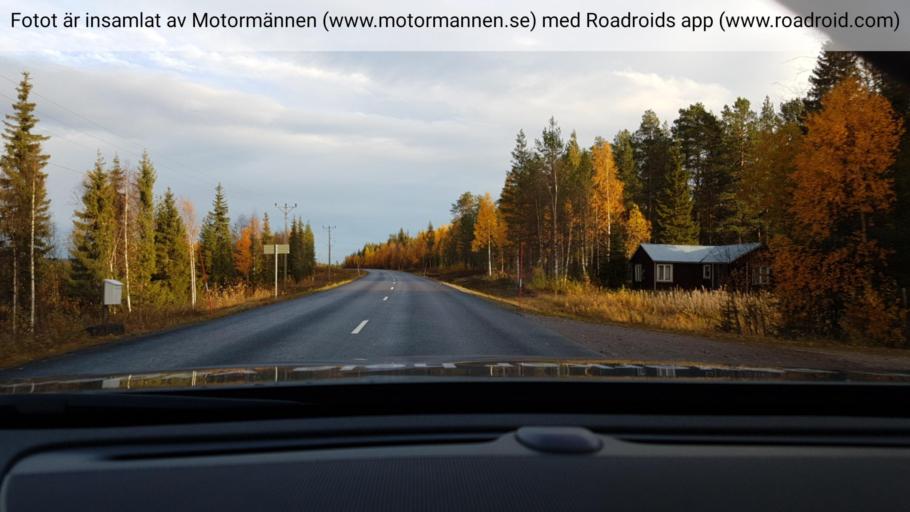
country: SE
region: Norrbotten
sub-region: Overkalix Kommun
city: OEverkalix
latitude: 66.9679
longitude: 22.6558
